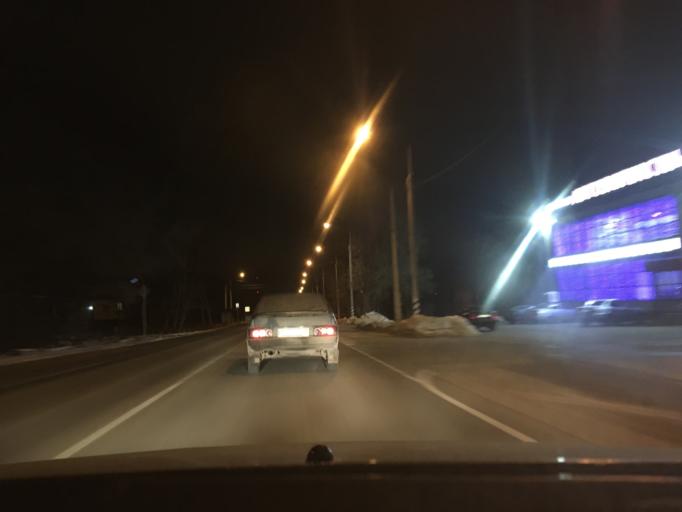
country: RU
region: Tula
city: Pervomayskiy
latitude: 54.0503
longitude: 37.5304
